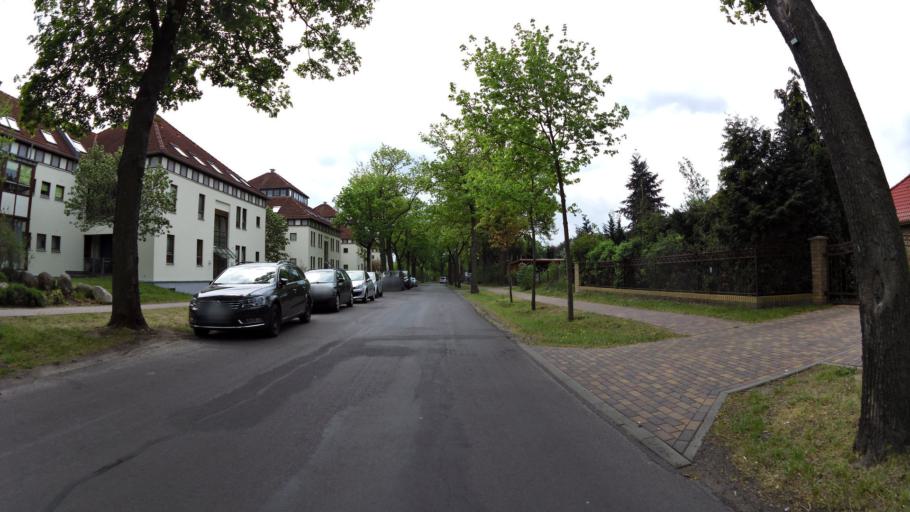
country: DE
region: Brandenburg
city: Schwerin
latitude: 52.2072
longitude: 13.5892
